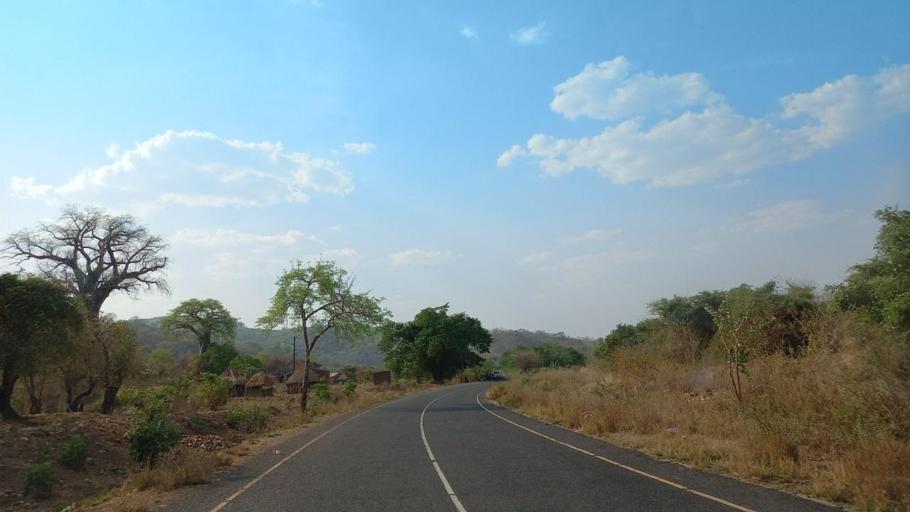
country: ZM
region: Lusaka
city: Luangwa
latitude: -15.0271
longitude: 30.2257
